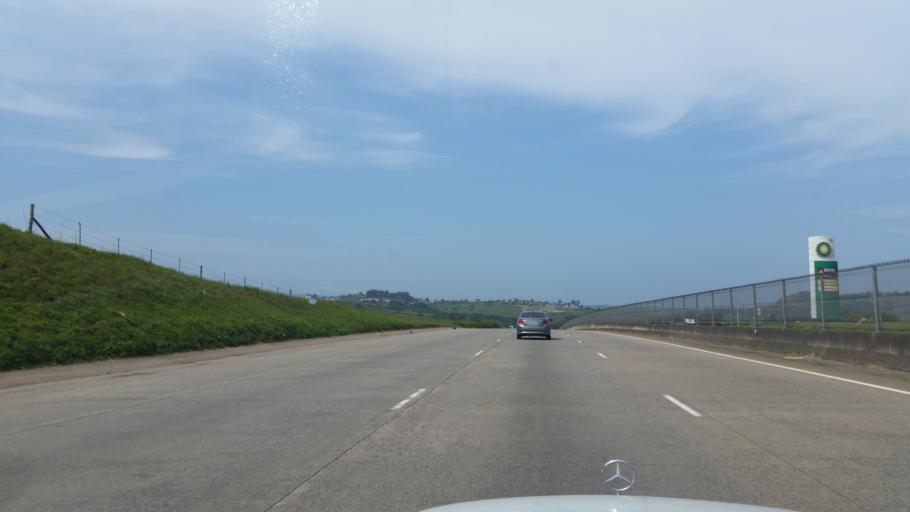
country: ZA
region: KwaZulu-Natal
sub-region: eThekwini Metropolitan Municipality
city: Mpumalanga
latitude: -29.7414
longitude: 30.6330
